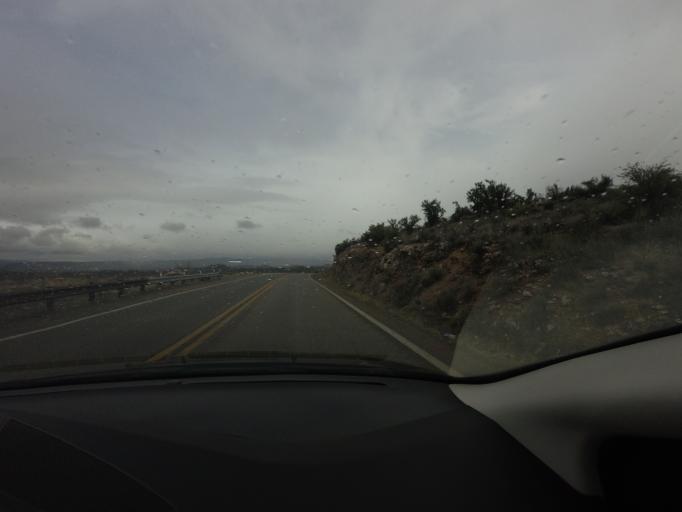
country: US
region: Arizona
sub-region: Yavapai County
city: Lake Montezuma
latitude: 34.6457
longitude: -111.8185
